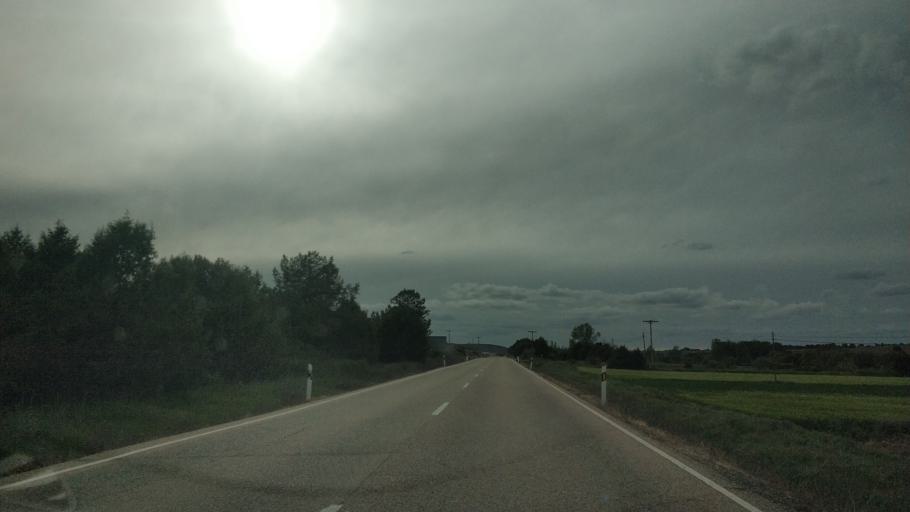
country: ES
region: Castille and Leon
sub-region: Provincia de Soria
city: Valdenebro
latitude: 41.5660
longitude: -2.9980
